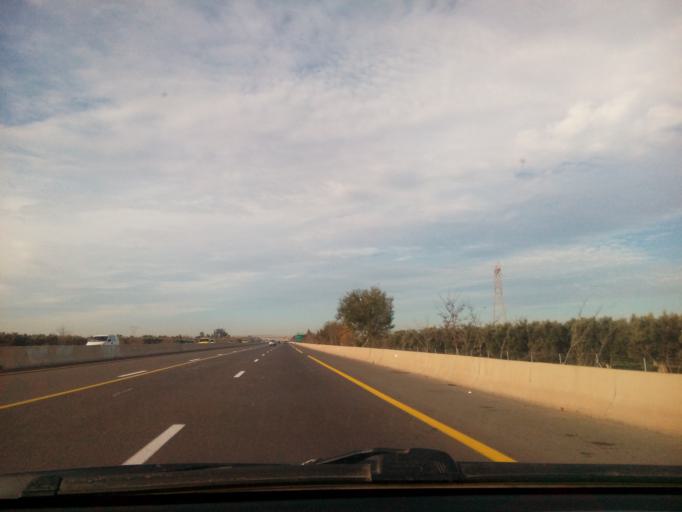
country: DZ
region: Mascara
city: Sig
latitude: 35.5815
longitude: -0.2307
